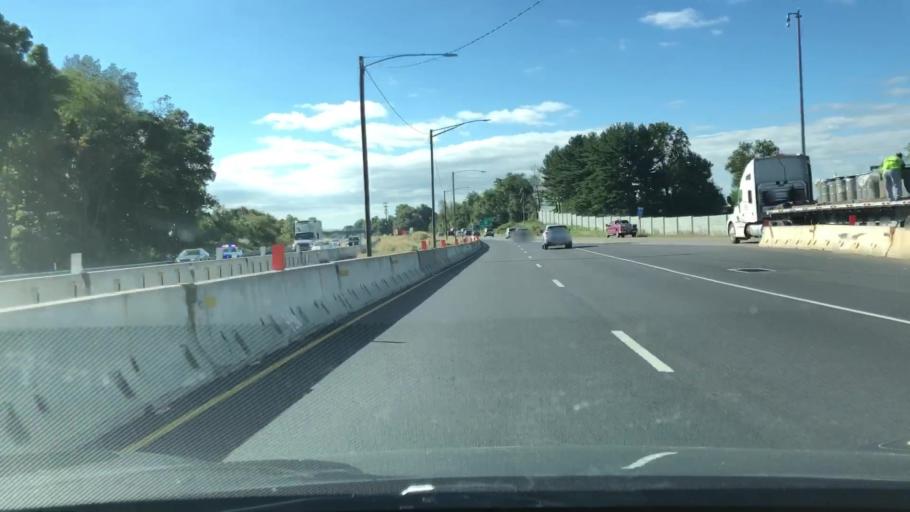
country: US
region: Pennsylvania
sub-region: Bucks County
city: Woodside
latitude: 40.2409
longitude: -74.8808
